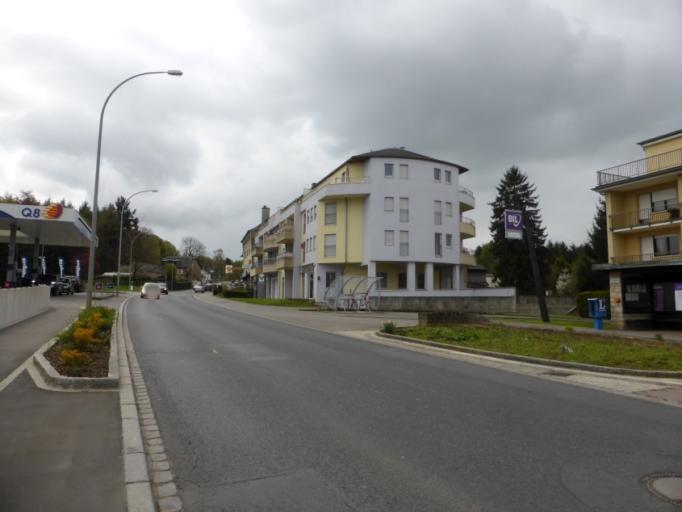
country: LU
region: Luxembourg
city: Bridel
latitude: 49.6578
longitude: 6.0818
